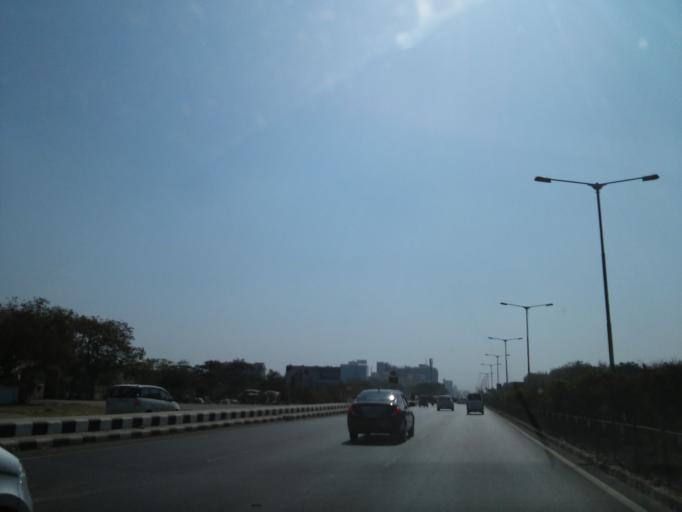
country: IN
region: Gujarat
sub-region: Ahmadabad
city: Ahmedabad
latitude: 23.0839
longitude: 72.5274
